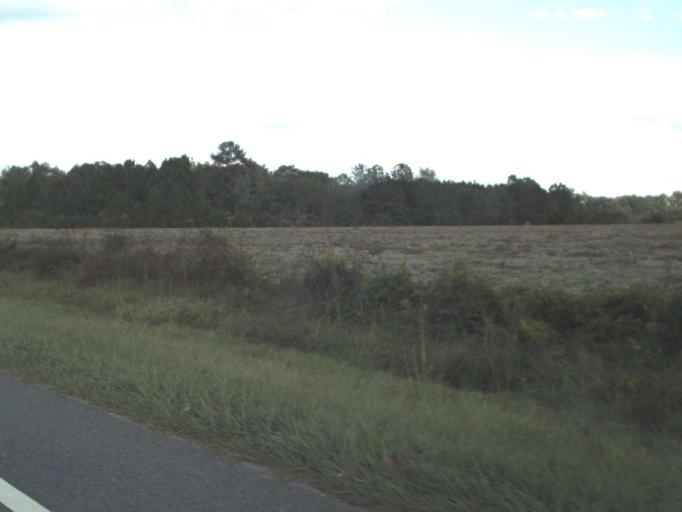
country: US
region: Florida
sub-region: Holmes County
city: Bonifay
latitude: 30.6757
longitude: -85.6394
